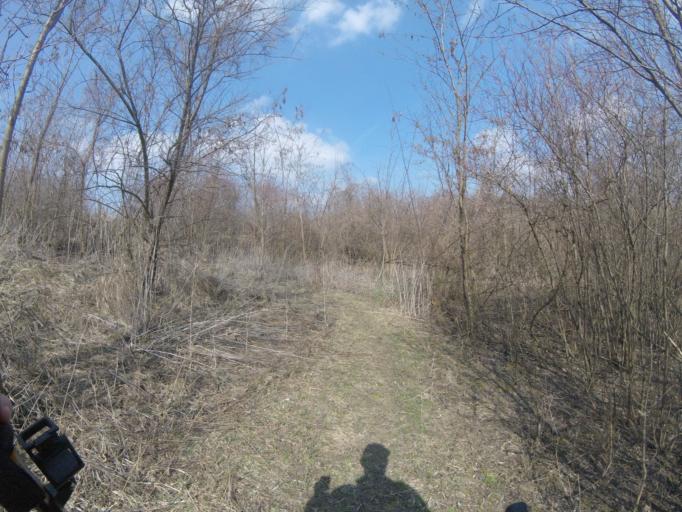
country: HU
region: Komarom-Esztergom
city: Nyergesujfalu
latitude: 47.7321
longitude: 18.5564
